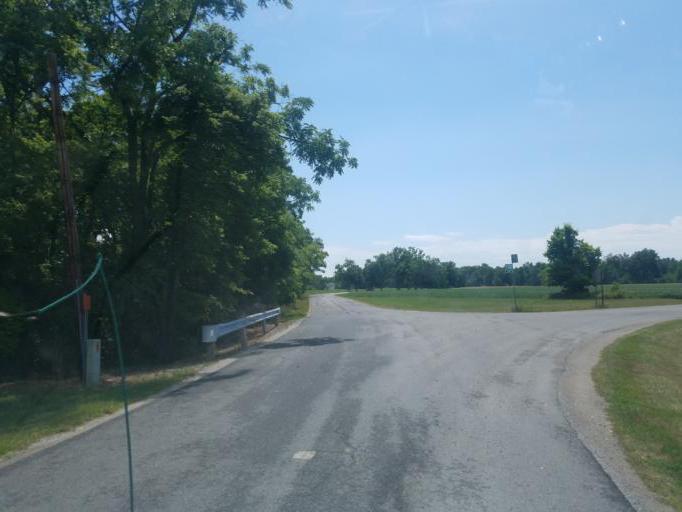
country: US
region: Ohio
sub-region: Paulding County
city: Antwerp
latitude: 41.1790
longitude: -84.7901
